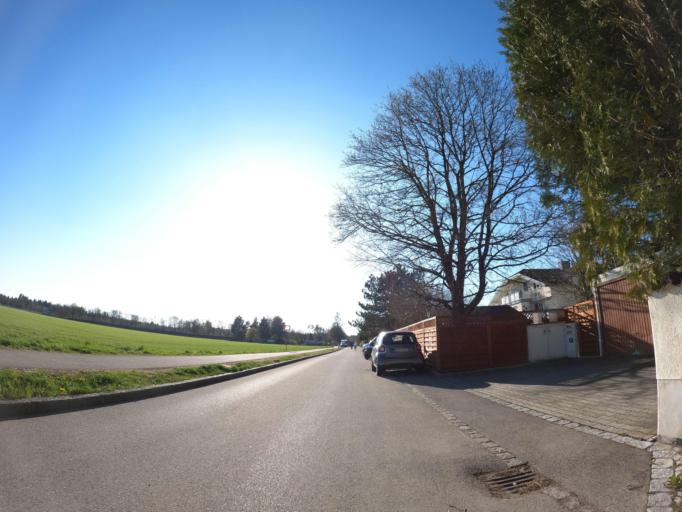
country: DE
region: Bavaria
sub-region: Upper Bavaria
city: Unterhaching
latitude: 48.0675
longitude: 11.6010
